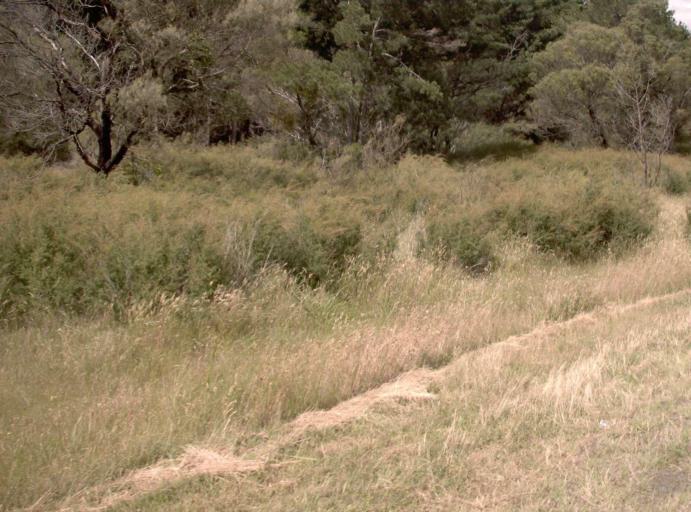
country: AU
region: Victoria
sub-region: Wellington
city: Sale
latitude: -38.1714
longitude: 146.9780
